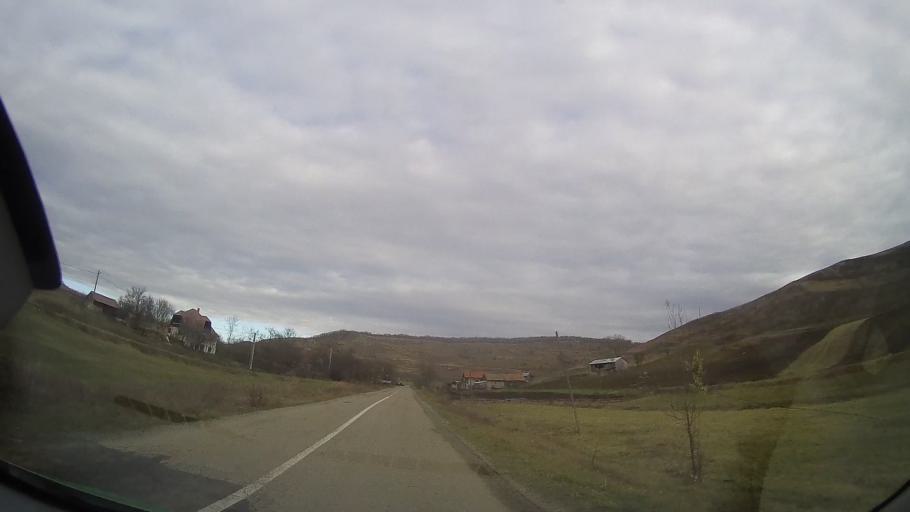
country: RO
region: Bistrita-Nasaud
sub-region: Comuna Micestii de Campie
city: Micestii de Campie
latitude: 46.8352
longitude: 24.3027
